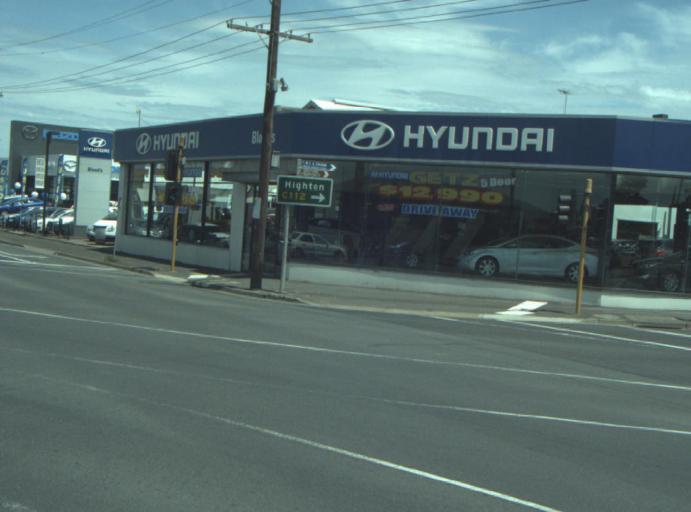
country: AU
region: Victoria
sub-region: Greater Geelong
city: Geelong
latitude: -38.1602
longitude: 144.3503
